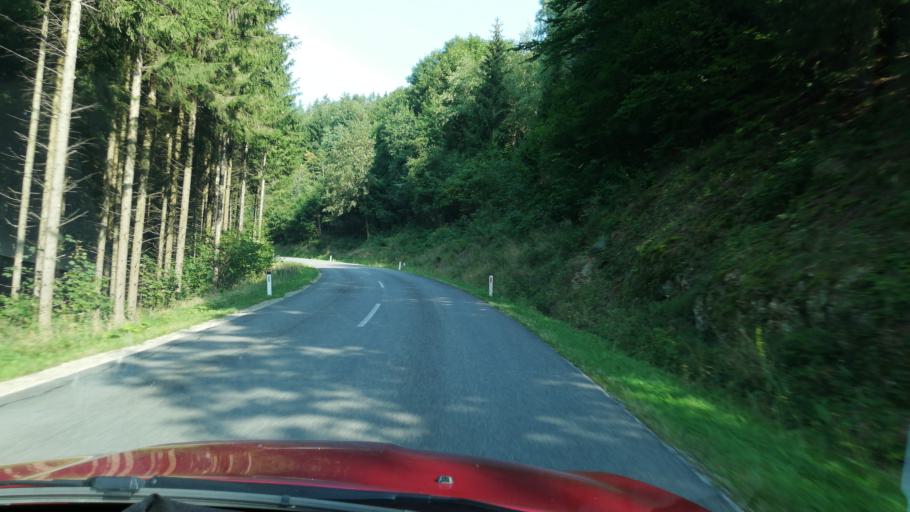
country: AT
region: Lower Austria
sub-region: Politischer Bezirk Zwettl
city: Langschlag
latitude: 48.4633
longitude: 14.7977
